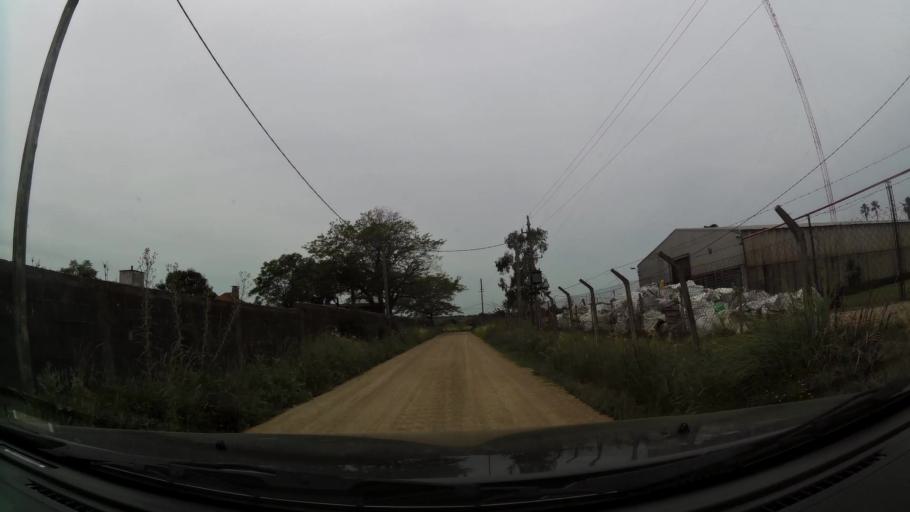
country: UY
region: Canelones
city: La Paz
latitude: -34.7471
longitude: -56.2250
